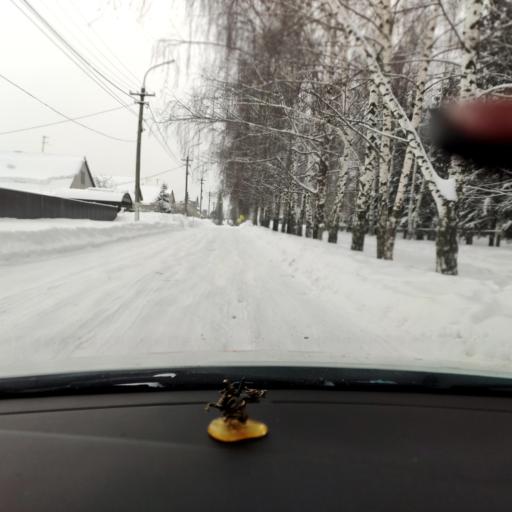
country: RU
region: Tatarstan
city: Stolbishchi
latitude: 55.6110
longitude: 49.1424
